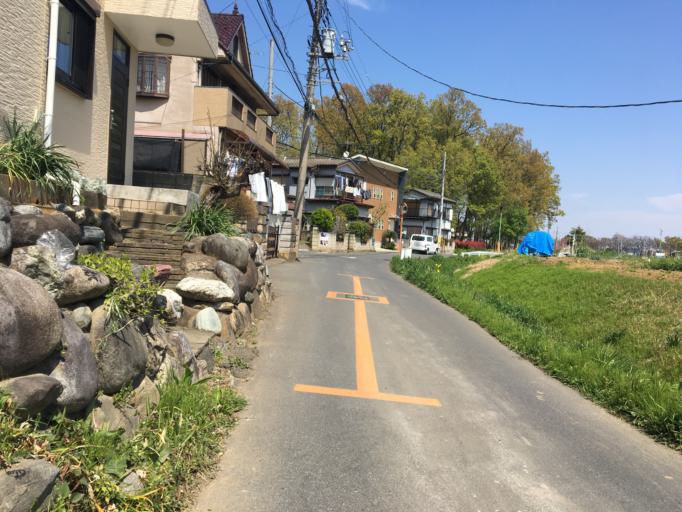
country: JP
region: Saitama
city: Shiki
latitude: 35.8367
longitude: 139.5618
